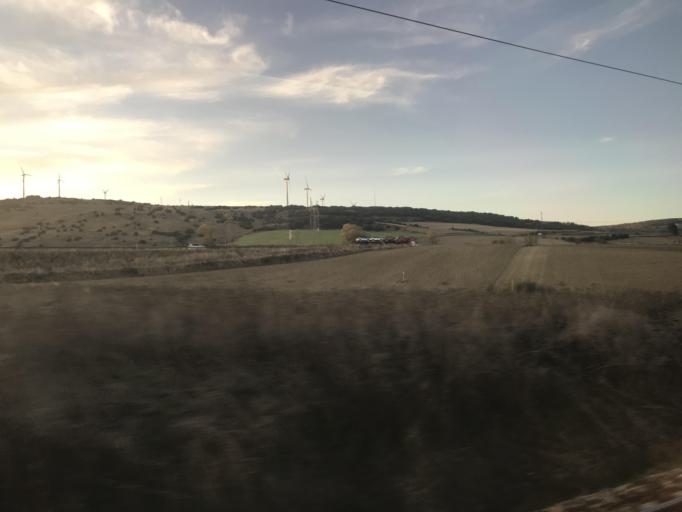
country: ES
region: Castille and Leon
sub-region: Provincia de Burgos
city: Monasterio de Rodilla
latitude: 42.4585
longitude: -3.4506
